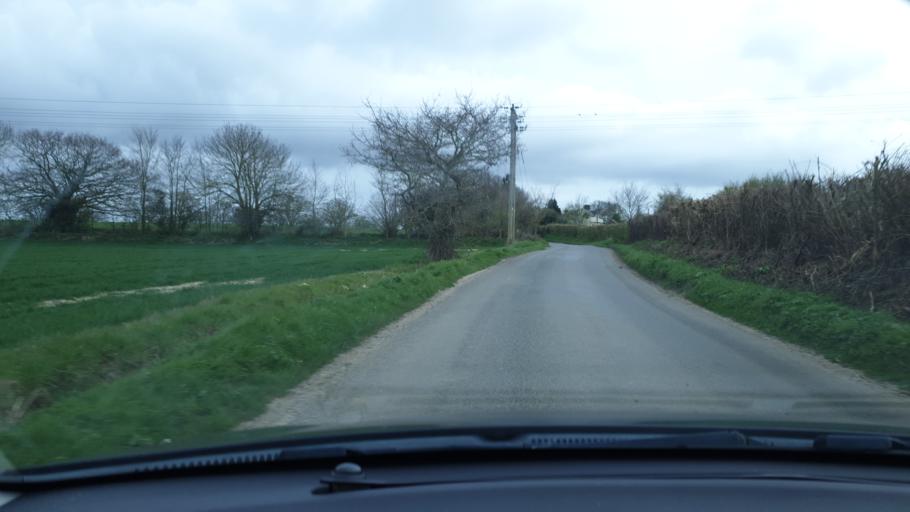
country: GB
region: England
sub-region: Suffolk
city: Shotley Gate
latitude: 51.9286
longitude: 1.1780
